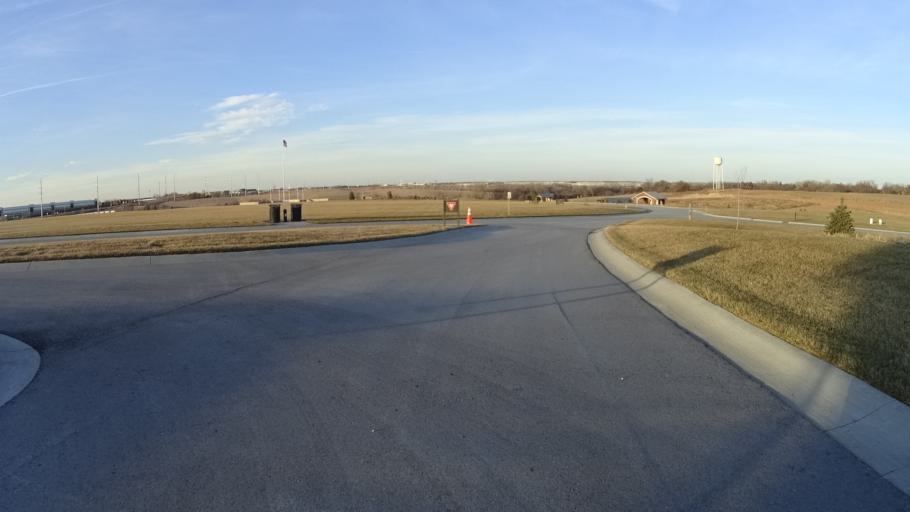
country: US
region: Nebraska
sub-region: Sarpy County
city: Chalco
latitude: 41.1349
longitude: -96.1322
